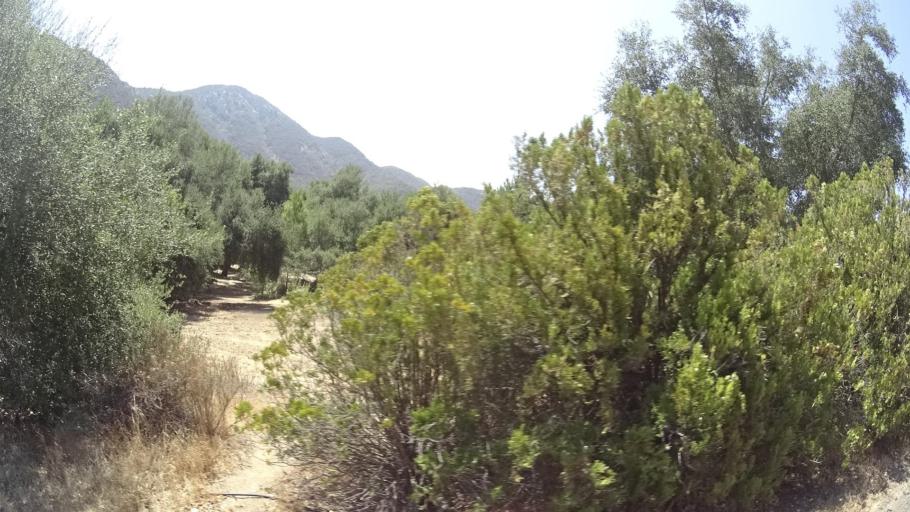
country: US
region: California
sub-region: San Diego County
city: Fallbrook
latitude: 33.4619
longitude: -117.2846
